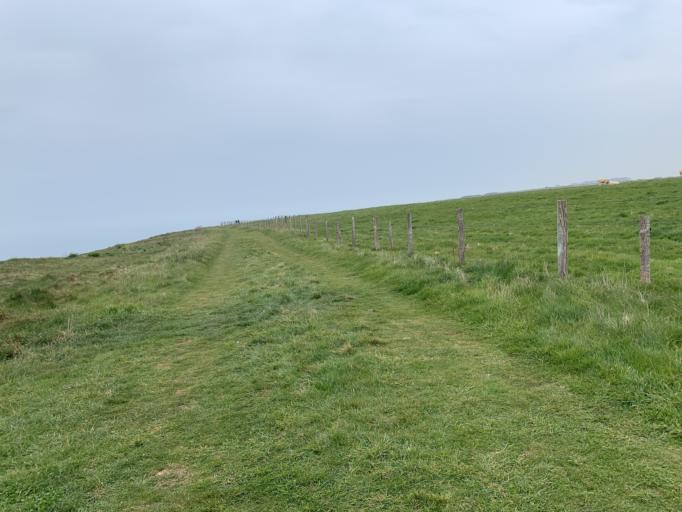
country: FR
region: Haute-Normandie
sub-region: Departement de la Seine-Maritime
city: Saint-Jouin-Bruneval
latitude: 49.6845
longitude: 0.1642
